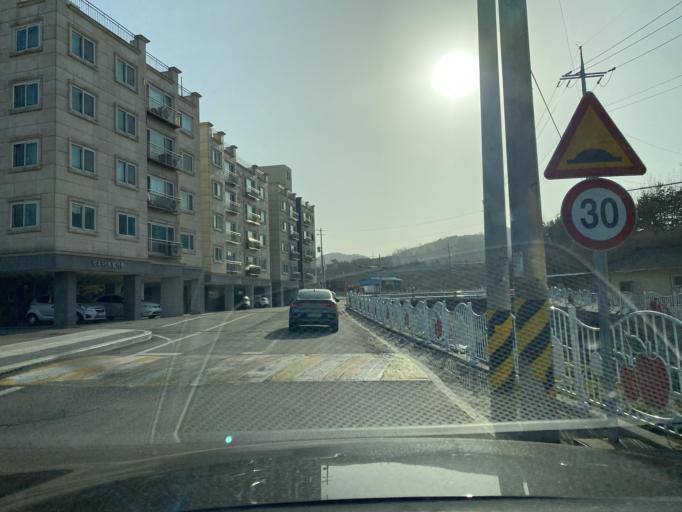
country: KR
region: Chungcheongnam-do
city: Yesan
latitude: 36.6755
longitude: 126.8496
